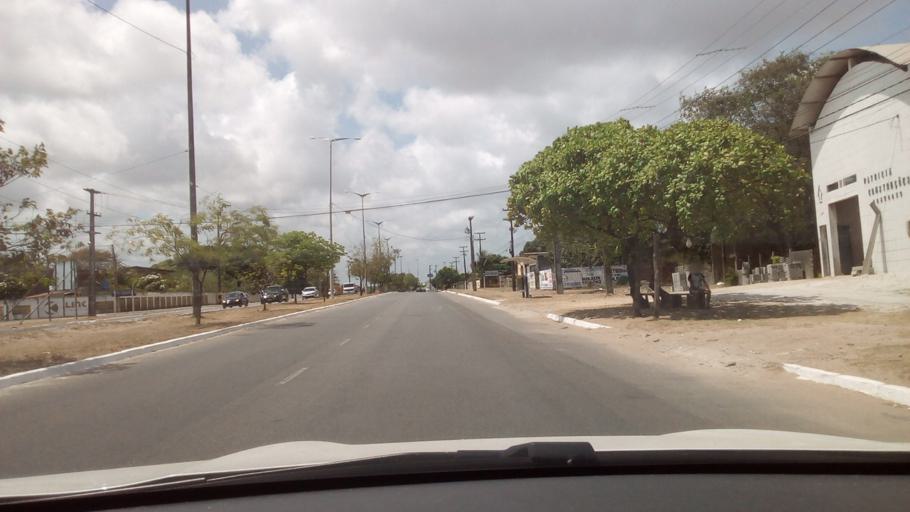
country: BR
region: Paraiba
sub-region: Joao Pessoa
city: Joao Pessoa
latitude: -7.1612
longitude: -34.8226
